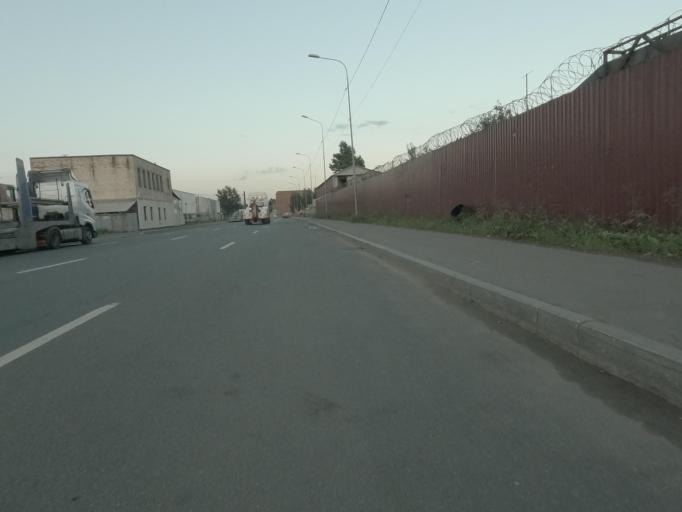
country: RU
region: St.-Petersburg
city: Vasyl'evsky Ostrov
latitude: 59.9034
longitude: 30.2390
